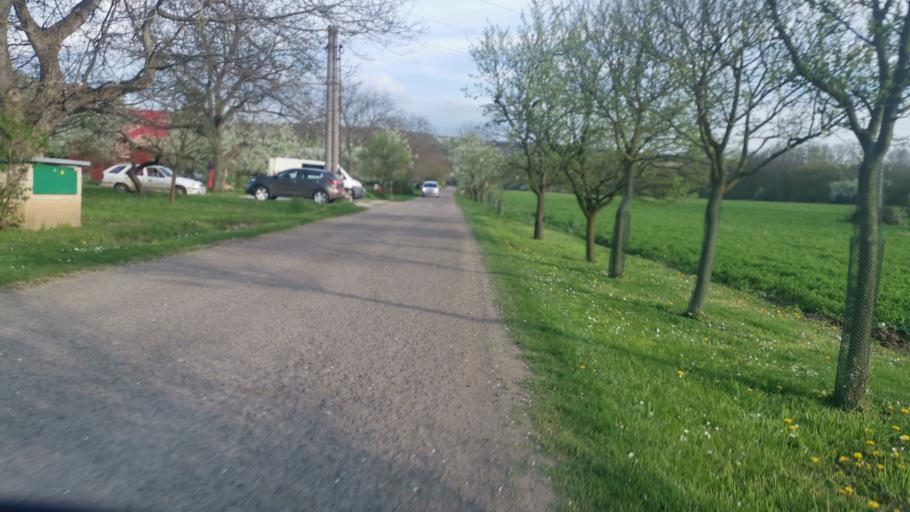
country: CZ
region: South Moravian
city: Petrov
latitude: 48.8480
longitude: 17.3017
